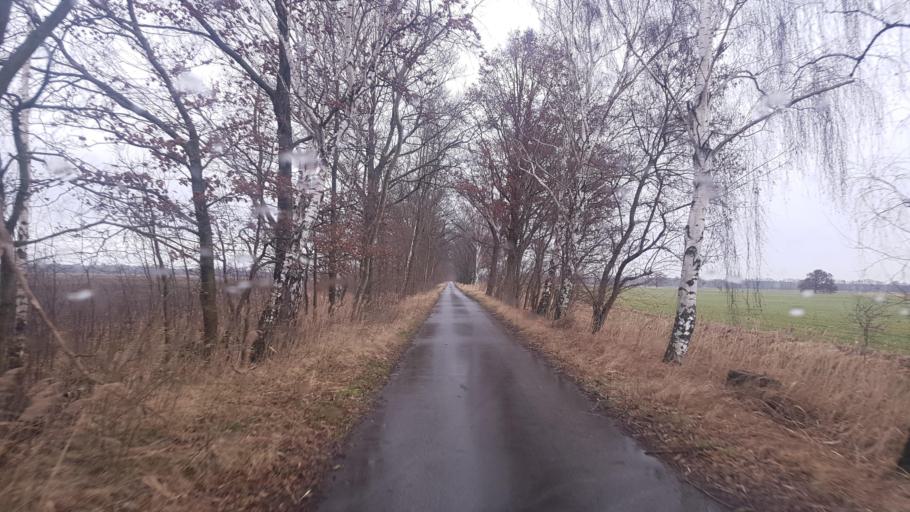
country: DE
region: Brandenburg
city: Grossthiemig
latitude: 51.4142
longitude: 13.6496
